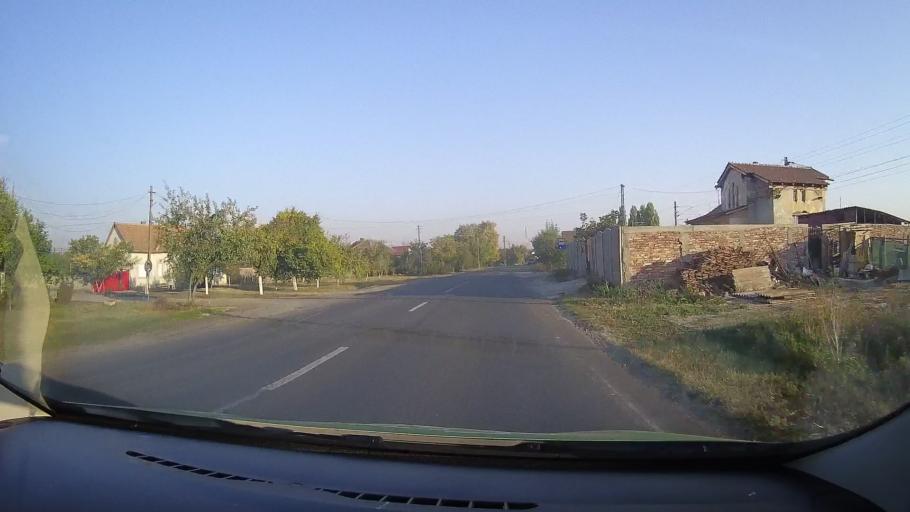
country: RO
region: Arad
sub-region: Comuna Sofronea
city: Sofronea
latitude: 46.2731
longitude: 21.3150
